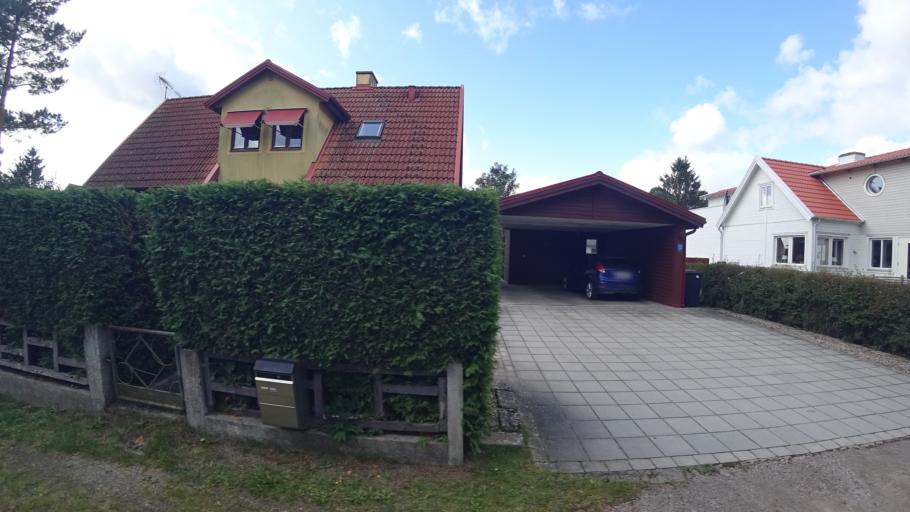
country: SE
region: Skane
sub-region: Kristianstads Kommun
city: Ahus
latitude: 55.9334
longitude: 14.3102
